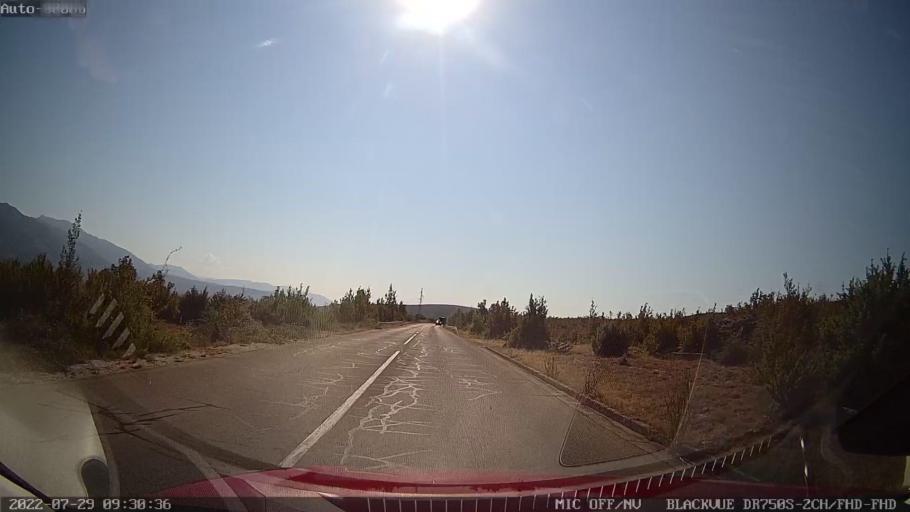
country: HR
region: Zadarska
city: Obrovac
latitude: 44.1933
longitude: 15.6880
